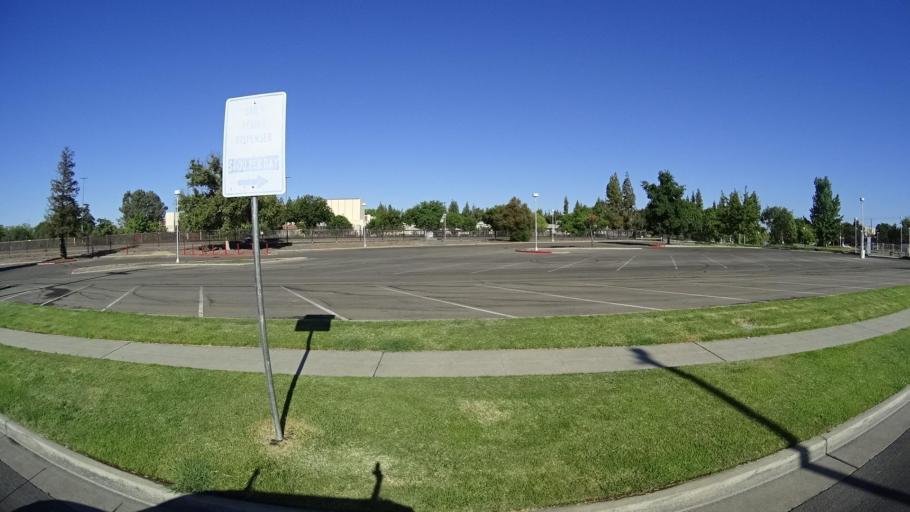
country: US
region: California
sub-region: Fresno County
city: Fresno
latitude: 36.7672
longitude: -119.7921
